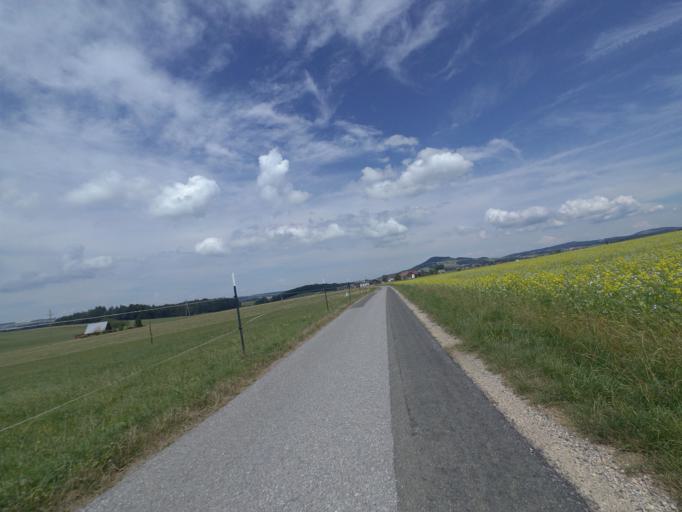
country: AT
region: Salzburg
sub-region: Politischer Bezirk Salzburg-Umgebung
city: Obertrum am See
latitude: 47.9073
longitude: 13.0923
